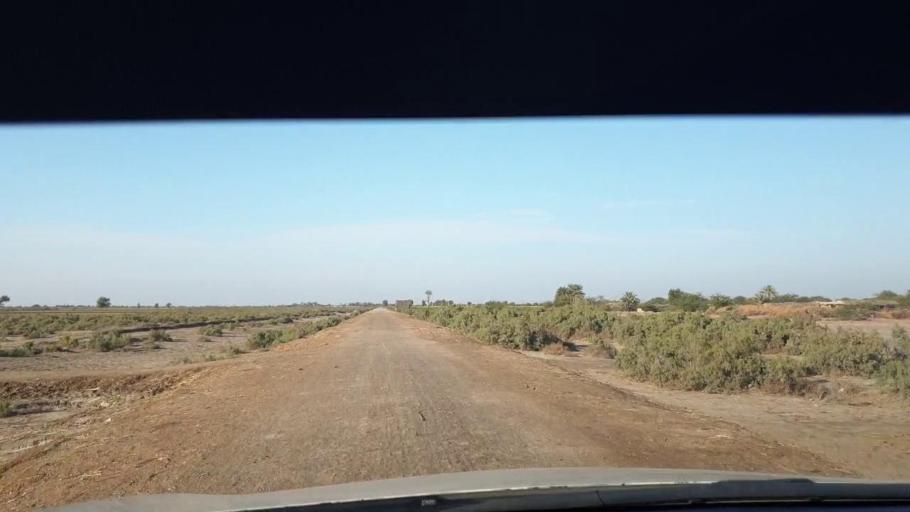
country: PK
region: Sindh
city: Berani
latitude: 25.8079
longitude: 68.9103
